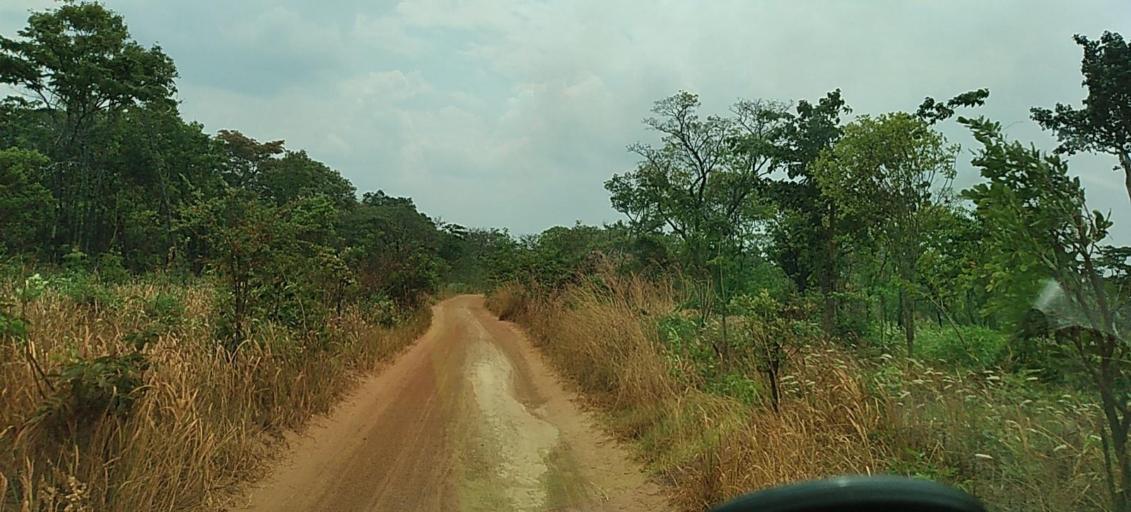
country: ZM
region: North-Western
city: Kansanshi
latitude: -12.0379
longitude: 26.3223
